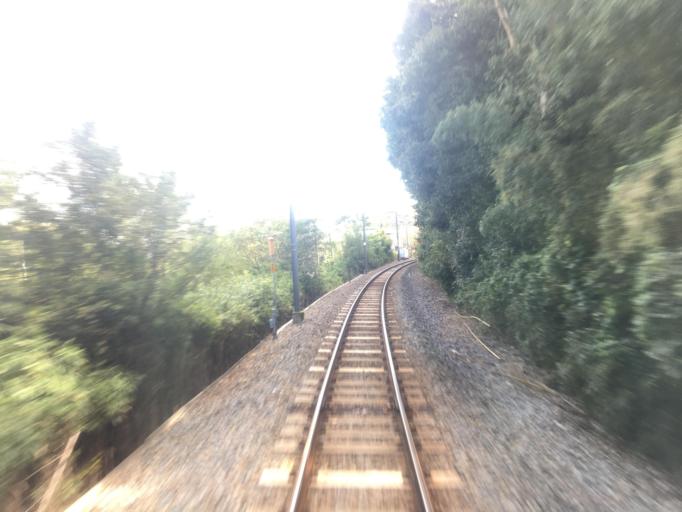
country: JP
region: Hyogo
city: Ono
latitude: 34.8279
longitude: 134.9274
